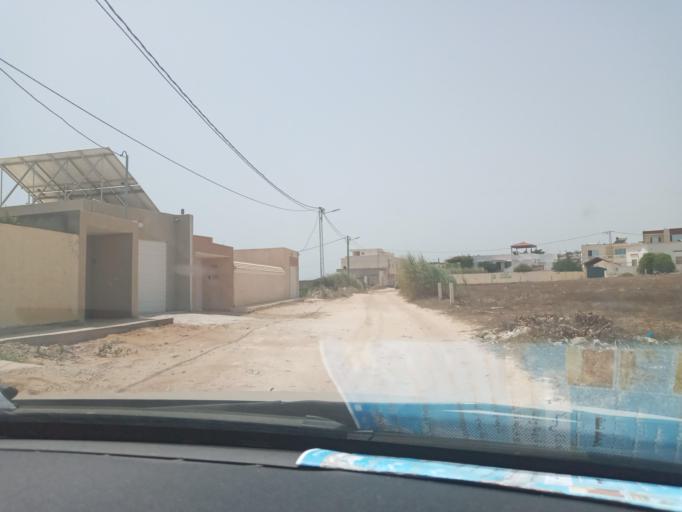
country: TN
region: Nabul
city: El Haouaria
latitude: 37.0292
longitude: 11.0562
